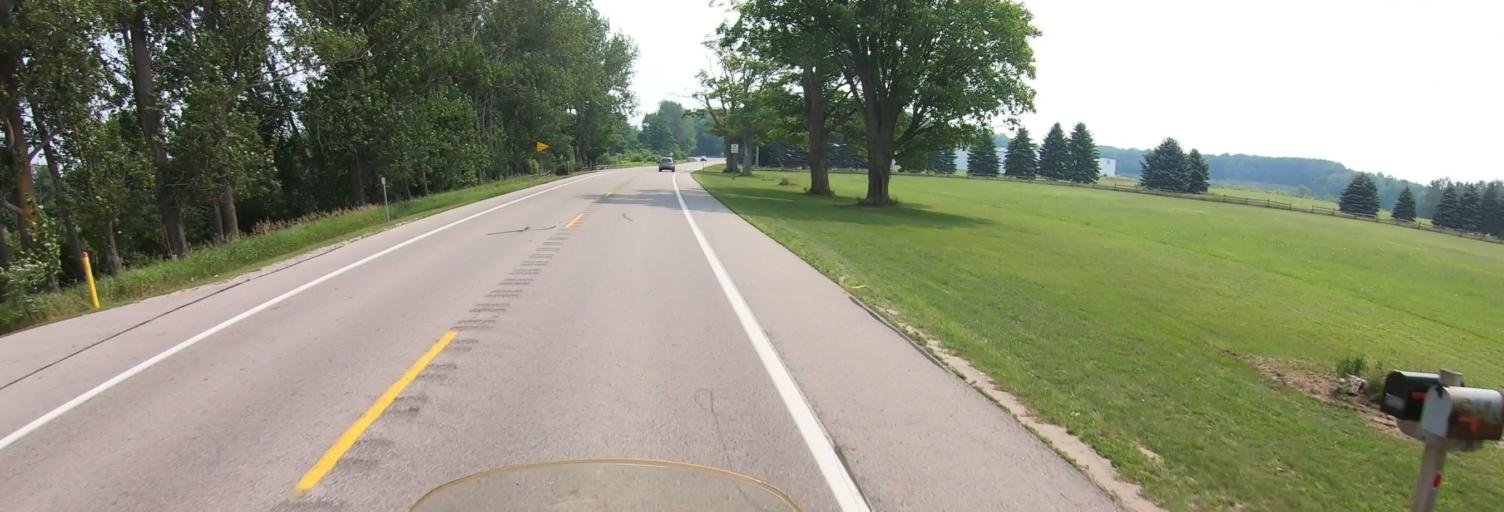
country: US
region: Michigan
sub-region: Leelanau County
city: Leland
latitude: 45.0889
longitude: -85.6011
